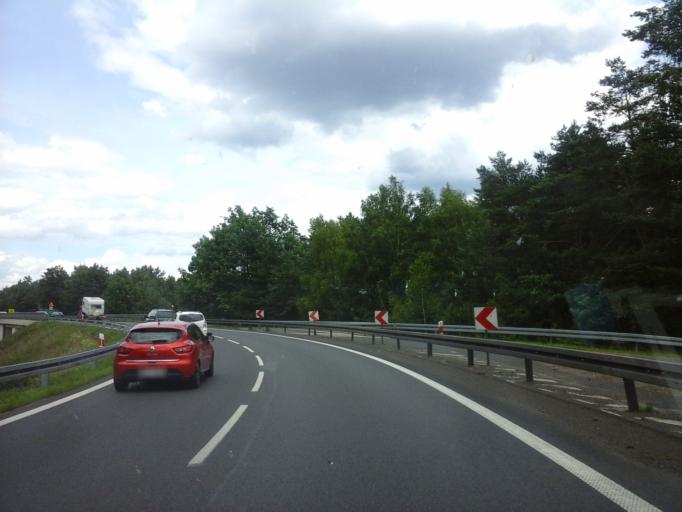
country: PL
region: West Pomeranian Voivodeship
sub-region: Powiat stargardzki
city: Kobylanka
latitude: 53.4234
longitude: 14.7727
